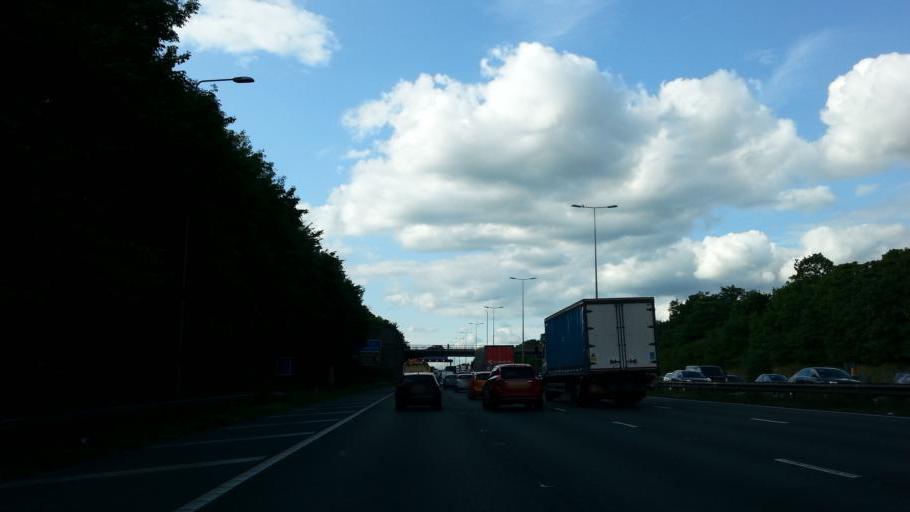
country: GB
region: England
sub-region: Leicestershire
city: Kirby Muxloe
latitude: 52.6240
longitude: -1.2094
